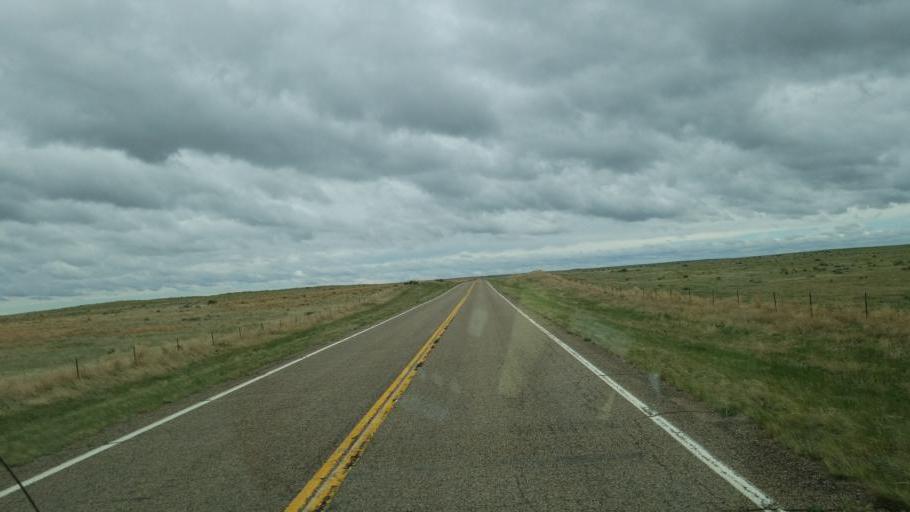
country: US
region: Colorado
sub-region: Lincoln County
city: Hugo
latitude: 38.8509
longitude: -103.5846
